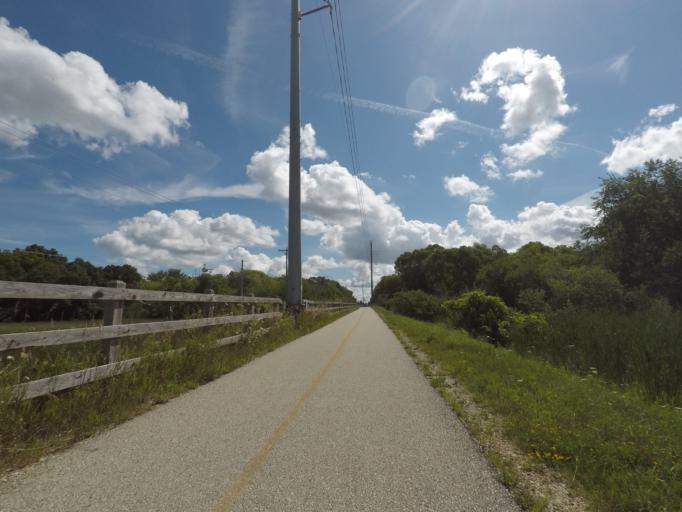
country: US
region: Wisconsin
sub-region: Waukesha County
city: Hartland
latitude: 43.0572
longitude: -88.3459
